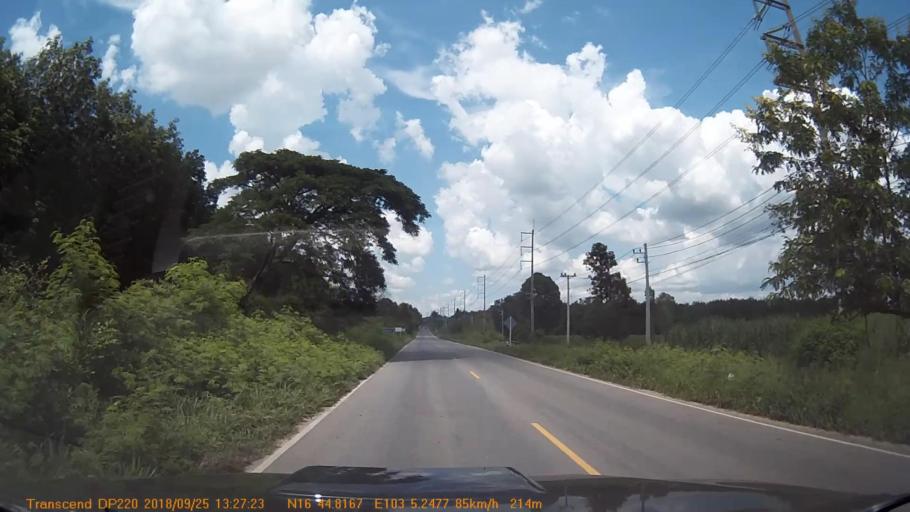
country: TH
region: Khon Kaen
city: Kranuan
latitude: 16.7468
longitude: 103.0874
